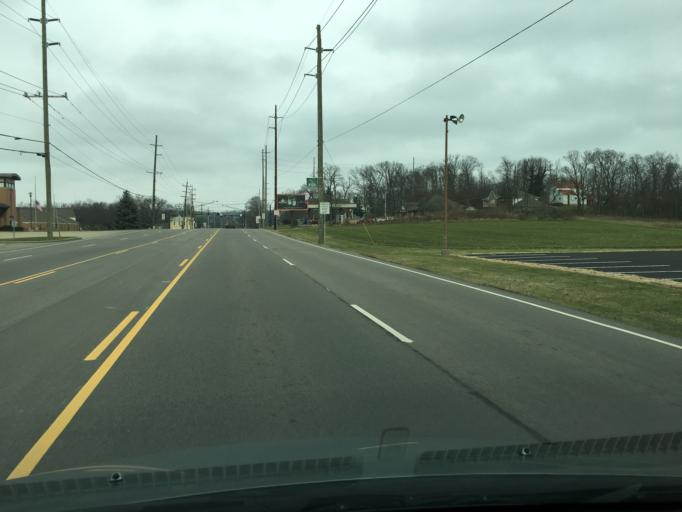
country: US
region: Ohio
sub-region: Butler County
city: Beckett Ridge
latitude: 39.3229
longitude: -84.4107
